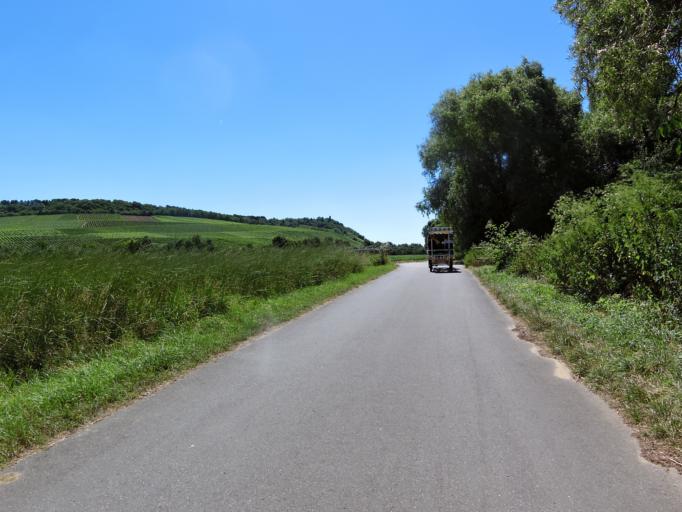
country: DE
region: Bavaria
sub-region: Regierungsbezirk Unterfranken
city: Sommerhausen
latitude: 49.6894
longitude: 10.0244
